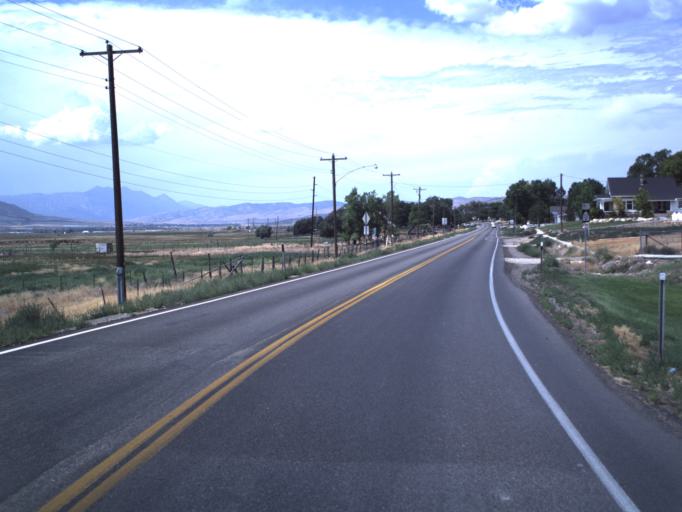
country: US
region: Utah
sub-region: Sanpete County
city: Moroni
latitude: 39.5255
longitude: -111.5905
